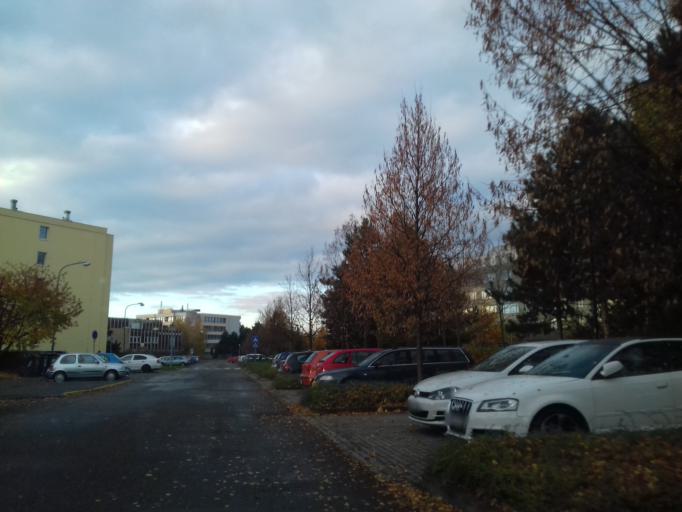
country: CZ
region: Olomoucky
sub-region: Okres Olomouc
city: Olomouc
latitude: 49.5925
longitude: 17.2651
